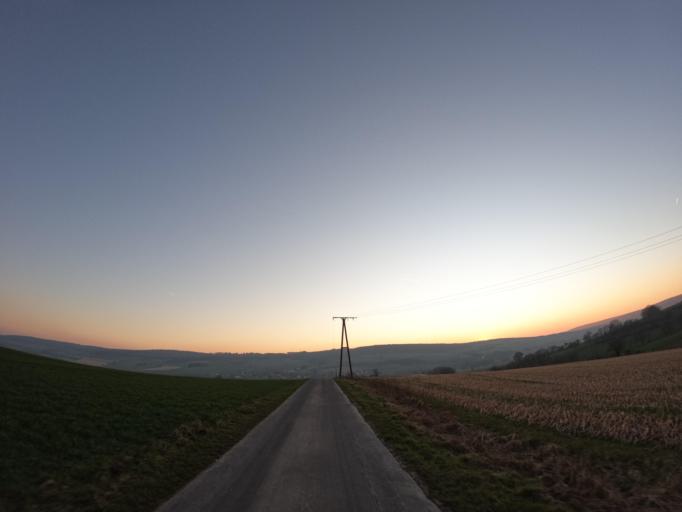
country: DE
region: Lower Saxony
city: Uslar
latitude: 51.6874
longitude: 9.5937
